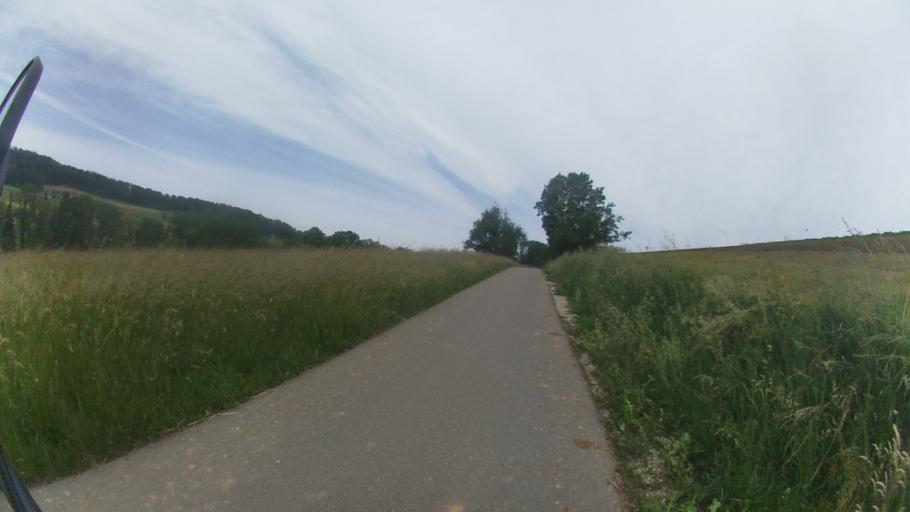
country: CH
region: Aargau
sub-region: Bezirk Baden
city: Unterehrendingen
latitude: 47.5093
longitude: 8.3288
